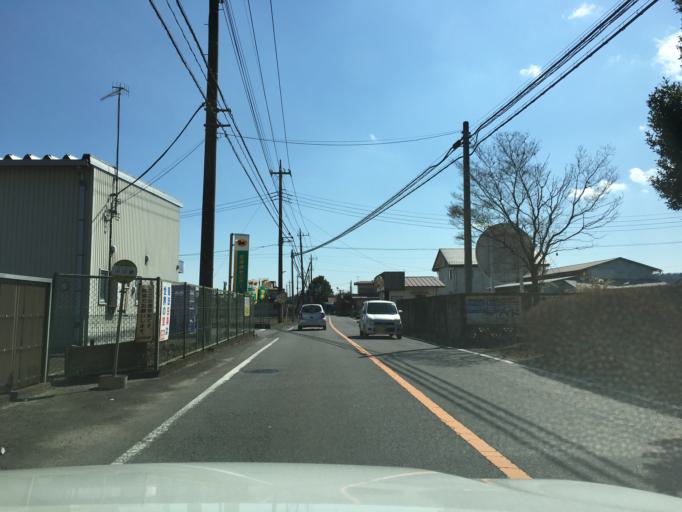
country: JP
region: Tochigi
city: Karasuyama
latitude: 36.7505
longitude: 140.1320
